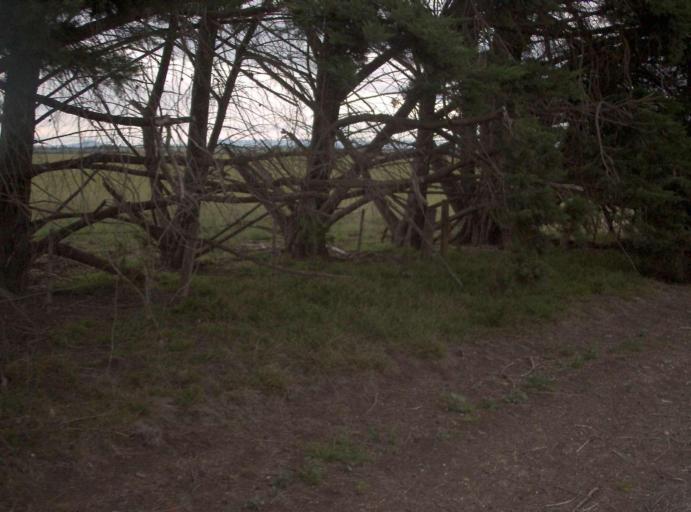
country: AU
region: Victoria
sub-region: Wellington
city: Sale
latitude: -38.0375
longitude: 147.1769
